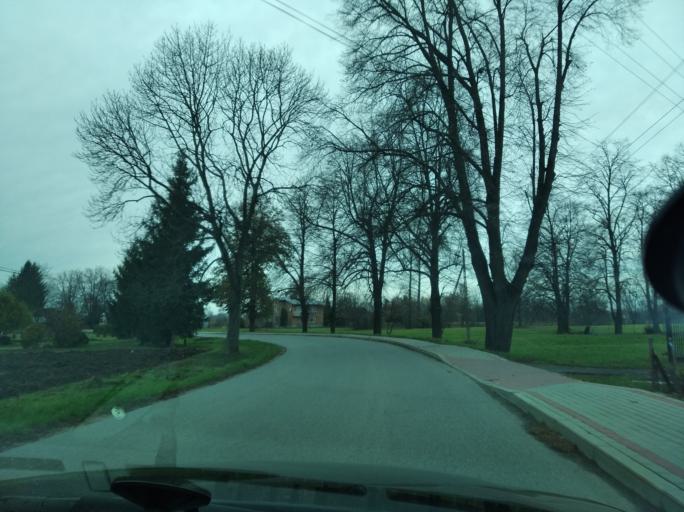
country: PL
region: Subcarpathian Voivodeship
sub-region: Powiat lancucki
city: Rogozno
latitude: 50.1000
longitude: 22.3780
